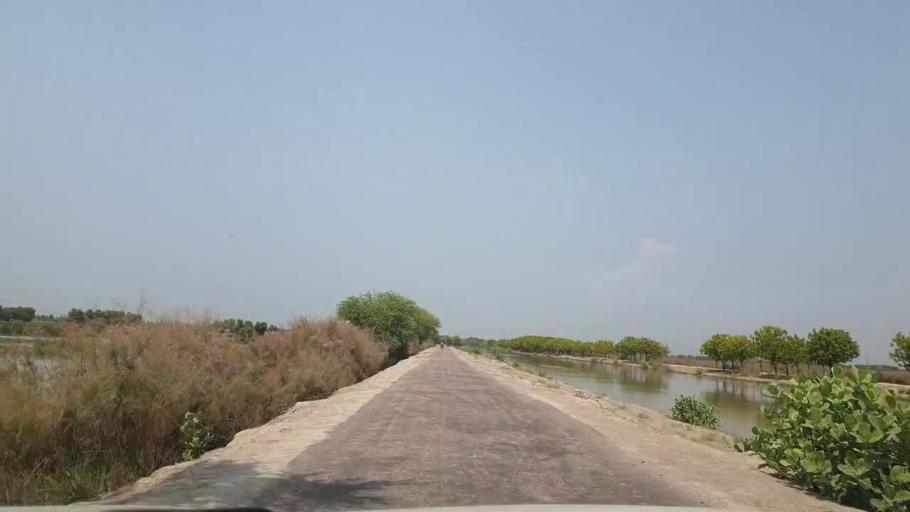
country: PK
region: Sindh
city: Dokri
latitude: 27.3502
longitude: 68.1123
